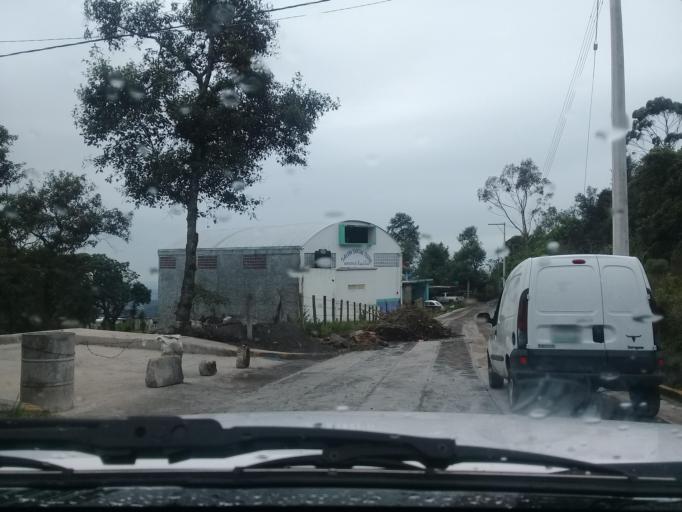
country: MX
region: Veracruz
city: Rafael Lucio
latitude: 19.6140
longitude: -96.9922
